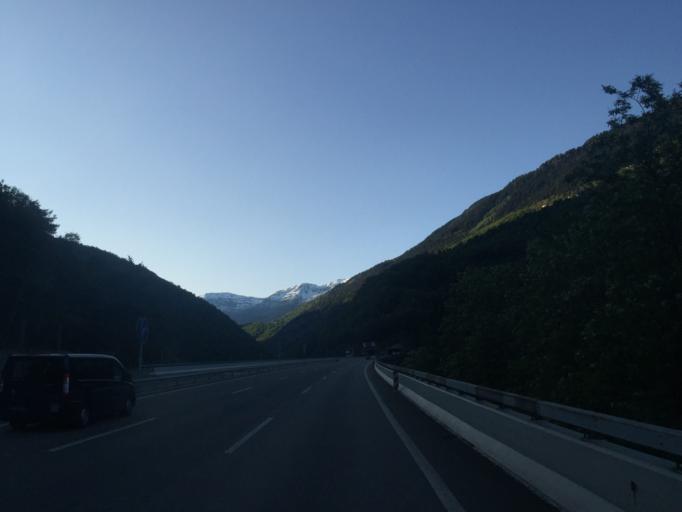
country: CH
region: Ticino
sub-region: Blenio District
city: Cancori
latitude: 46.4175
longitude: 8.8589
